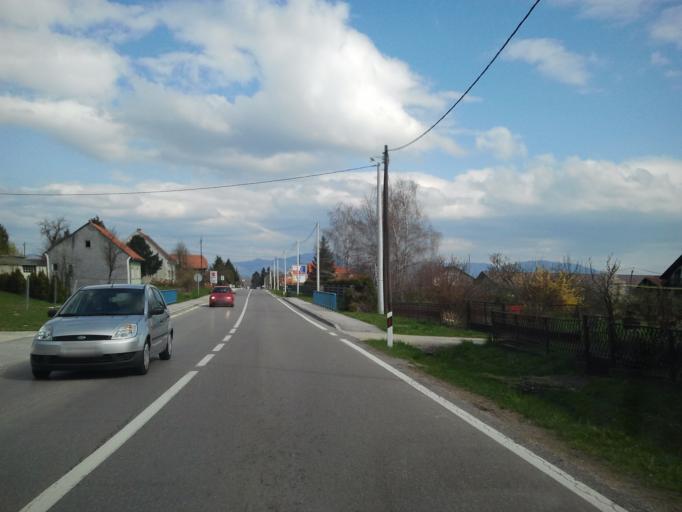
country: HR
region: Zagrebacka
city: Jastrebarsko
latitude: 45.5983
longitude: 15.5988
